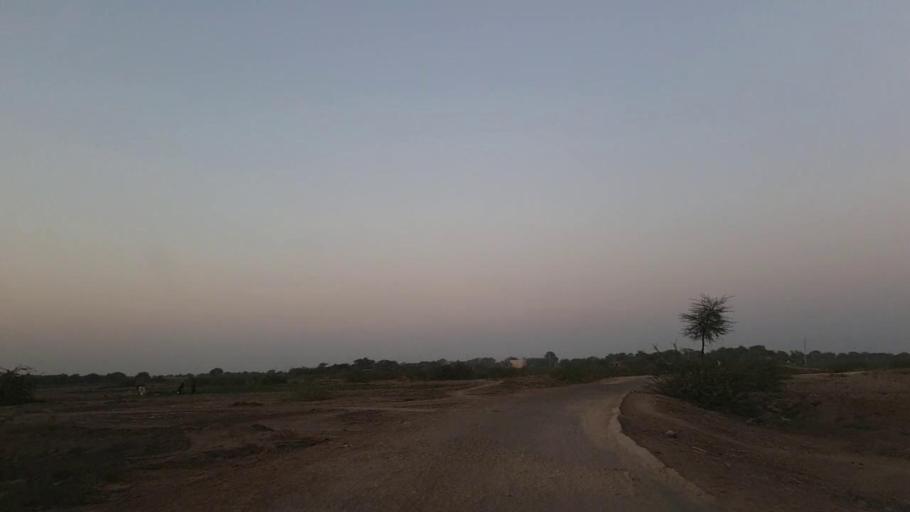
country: PK
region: Sindh
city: Naukot
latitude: 24.8696
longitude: 69.3838
